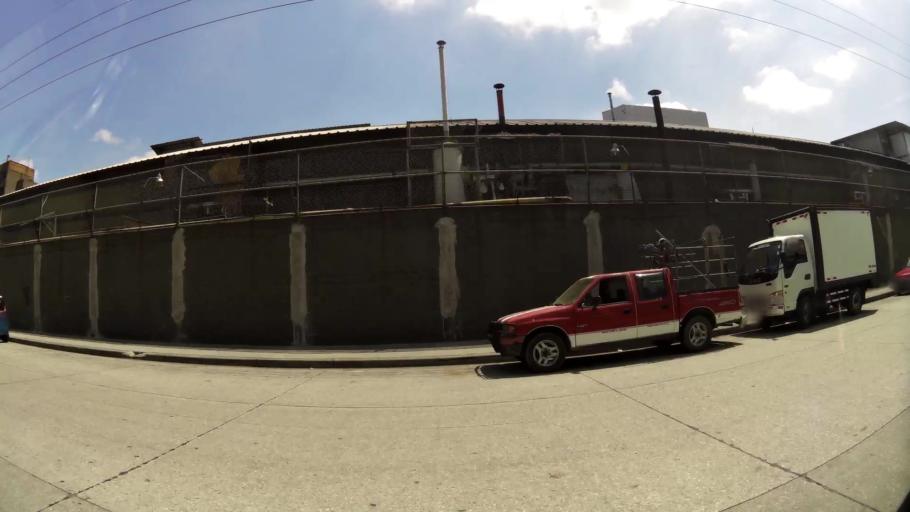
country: EC
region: Guayas
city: Eloy Alfaro
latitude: -2.1398
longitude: -79.9100
